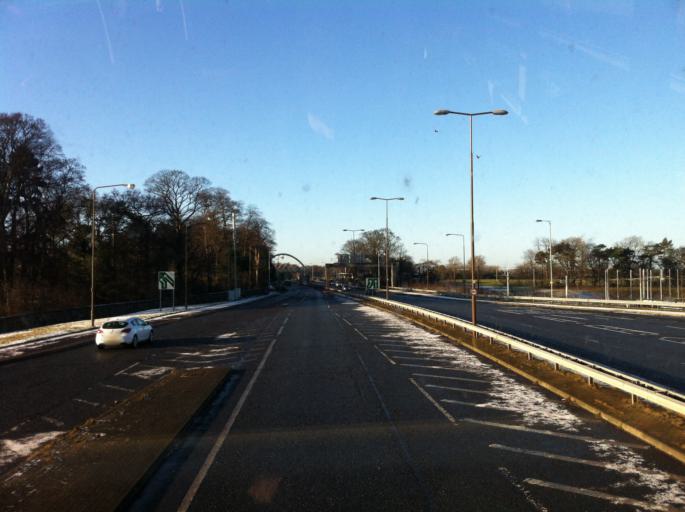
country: GB
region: Scotland
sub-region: Edinburgh
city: Currie
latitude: 55.9389
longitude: -3.3257
